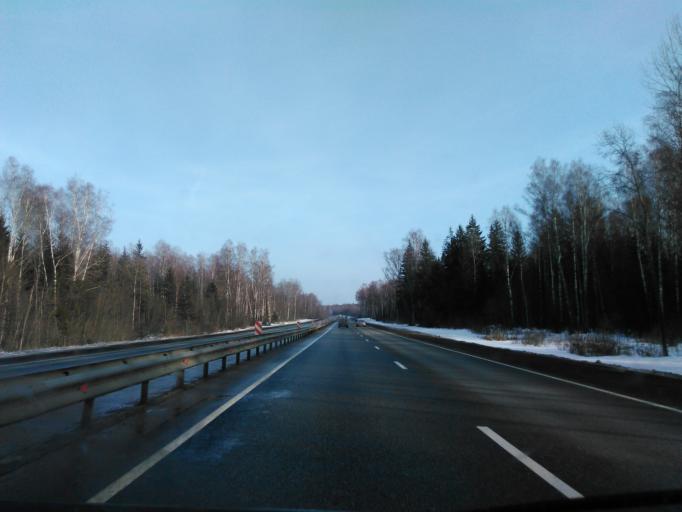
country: RU
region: Smolensk
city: Vyaz'ma
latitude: 55.1938
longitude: 33.9398
